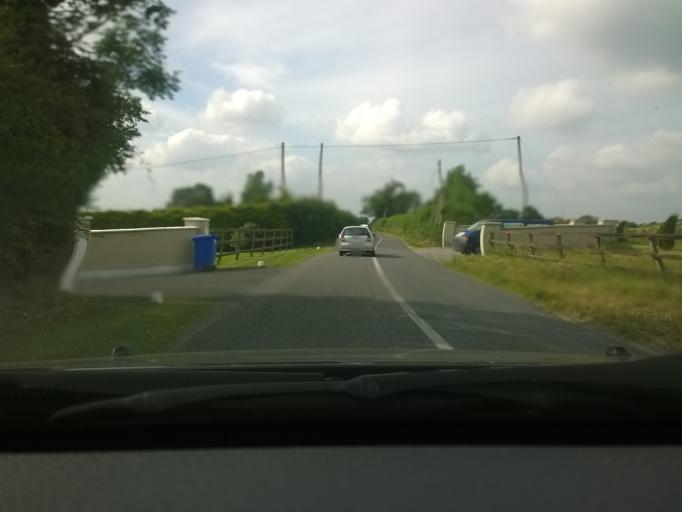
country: IE
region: Leinster
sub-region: Kildare
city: Cherryville
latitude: 53.1933
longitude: -6.9502
